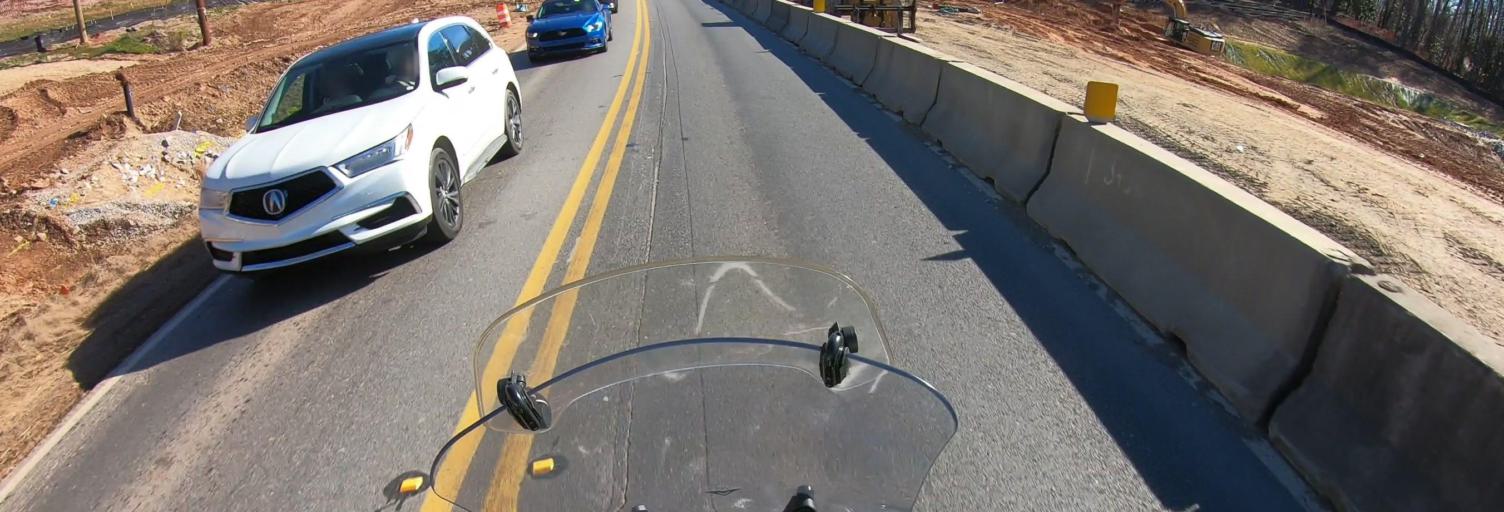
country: US
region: Georgia
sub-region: Cherokee County
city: Canton
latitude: 34.2360
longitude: -84.4508
